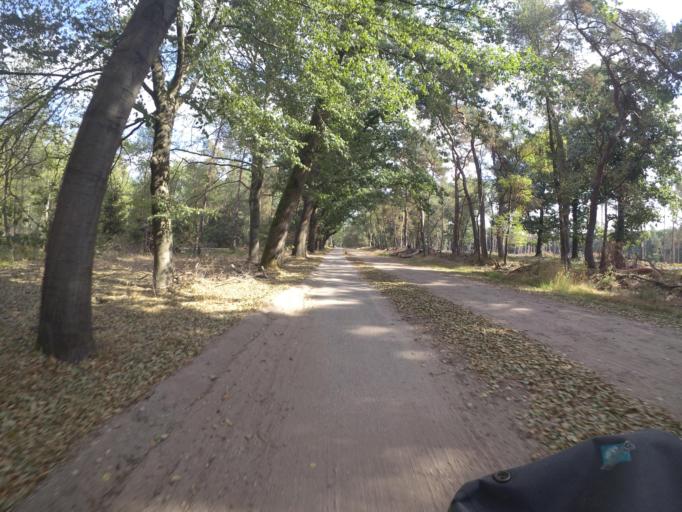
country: NL
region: Overijssel
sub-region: Gemeente Hof van Twente
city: Markelo
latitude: 52.3347
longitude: 6.4423
